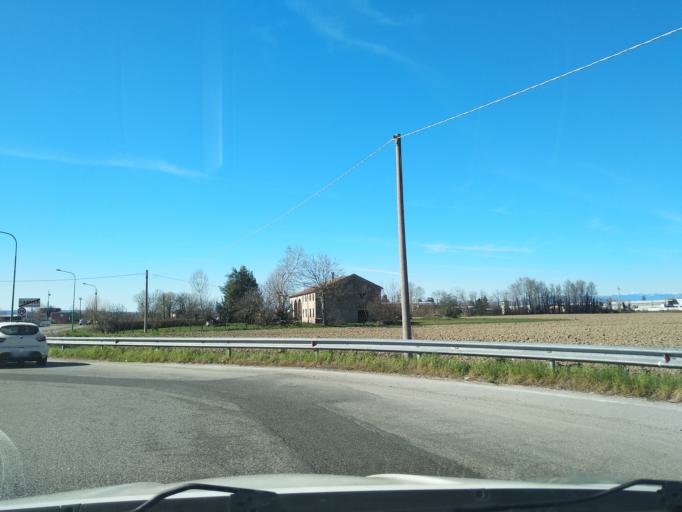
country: IT
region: Veneto
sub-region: Provincia di Padova
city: Caselle
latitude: 45.4138
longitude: 11.8041
